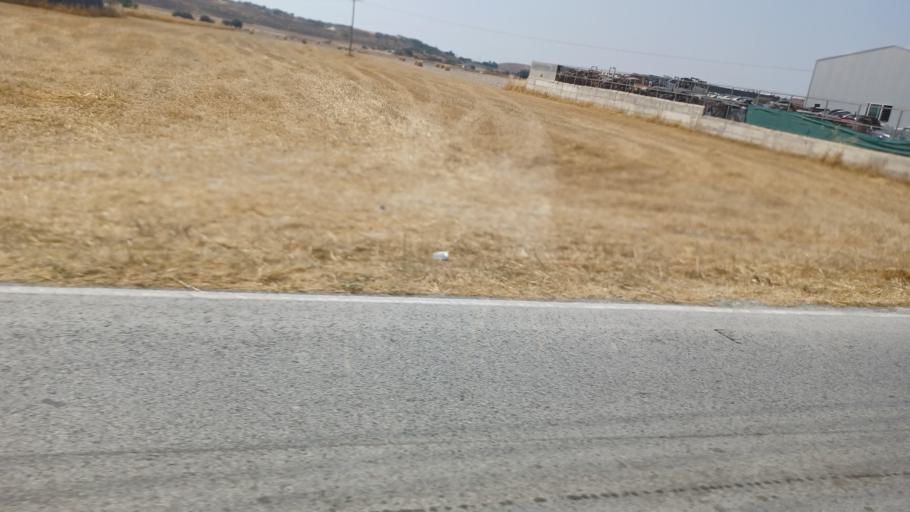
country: CY
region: Larnaka
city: Aradippou
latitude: 34.9324
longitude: 33.5442
